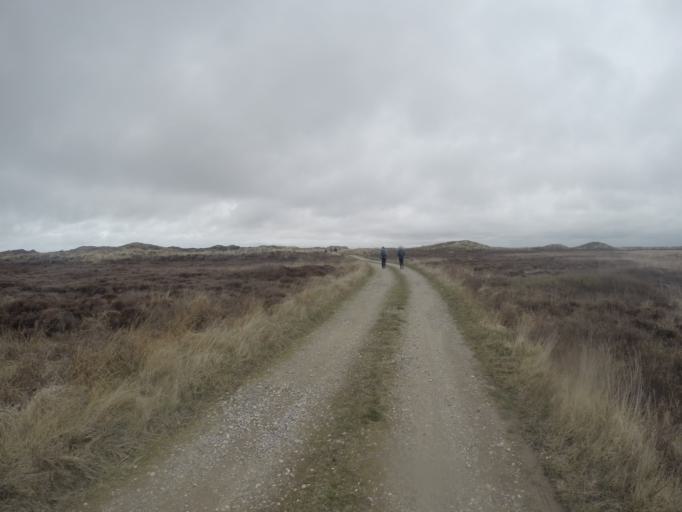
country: DK
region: North Denmark
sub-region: Thisted Kommune
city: Hurup
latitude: 56.8856
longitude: 8.3209
